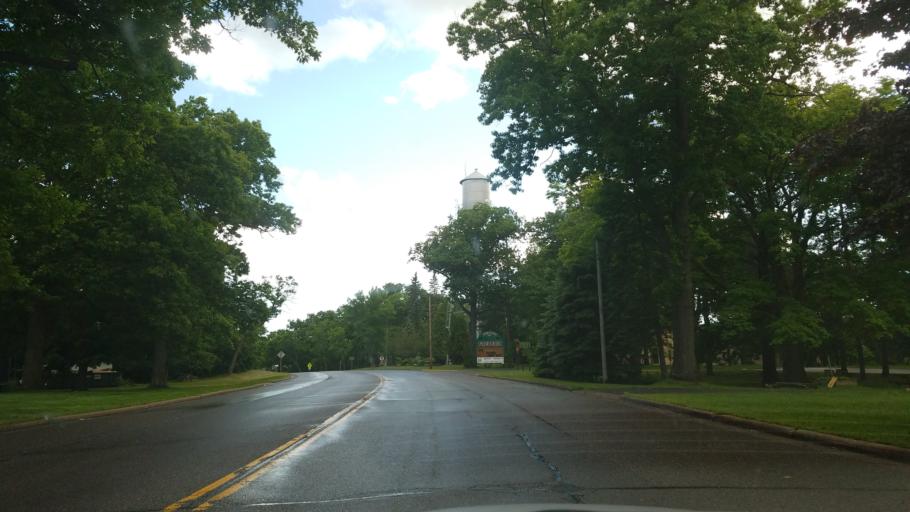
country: US
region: Wisconsin
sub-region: Polk County
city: Frederic
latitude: 45.6662
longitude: -92.4651
